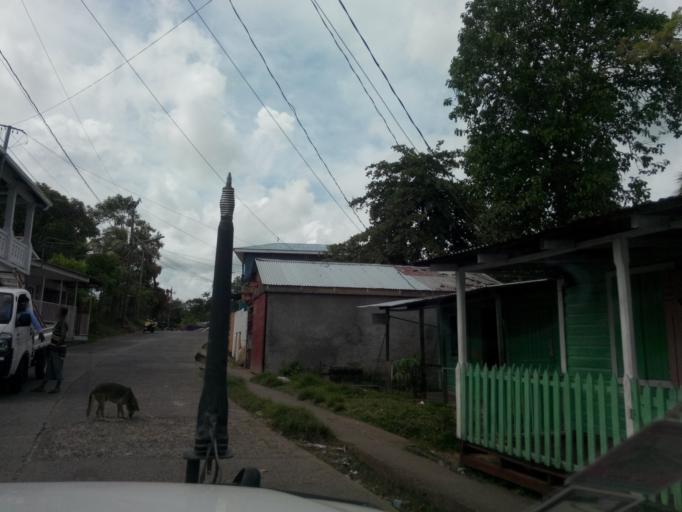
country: NI
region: Atlantico Sur
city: Bluefields
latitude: 12.0121
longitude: -83.7712
